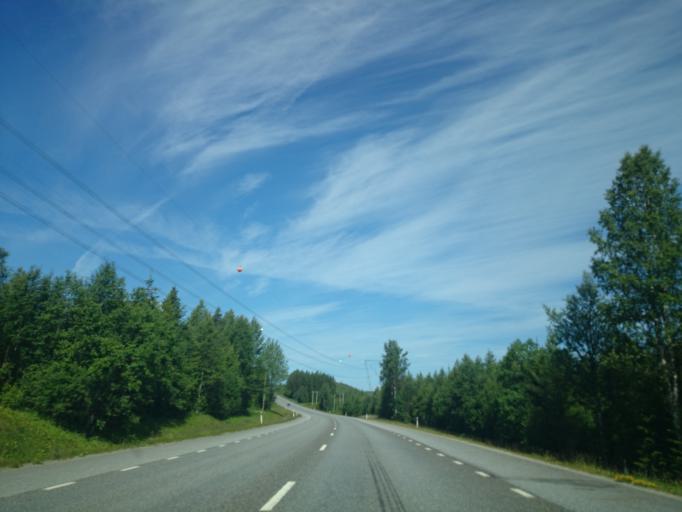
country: SE
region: Vaesternorrland
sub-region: Ange Kommun
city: Ange
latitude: 62.6720
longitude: 15.6034
